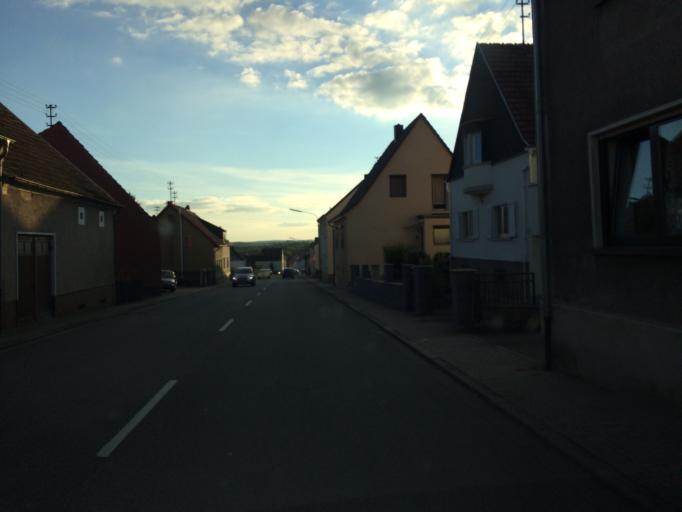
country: DE
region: Saarland
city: Bexbach
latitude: 49.3481
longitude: 7.2948
